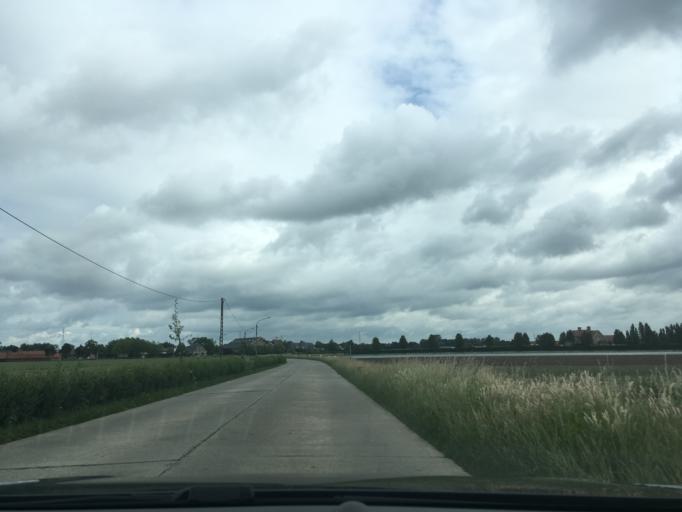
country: BE
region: Flanders
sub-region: Provincie West-Vlaanderen
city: Hooglede
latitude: 50.9488
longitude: 3.0600
